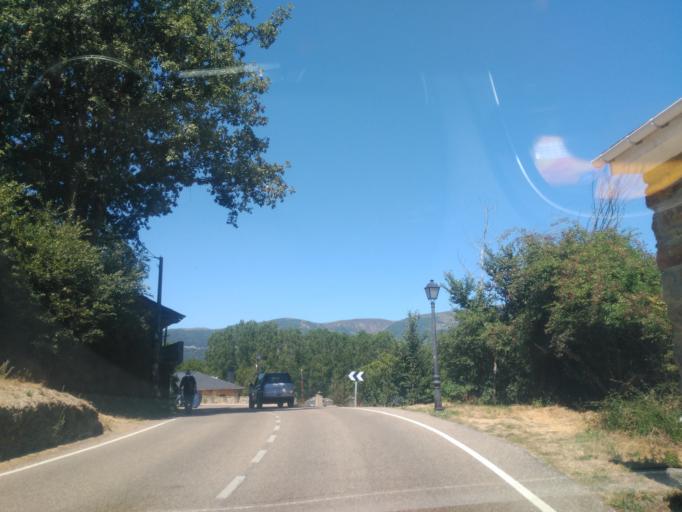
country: ES
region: Castille and Leon
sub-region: Provincia de Zamora
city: Galende
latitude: 42.1044
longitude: -6.6630
